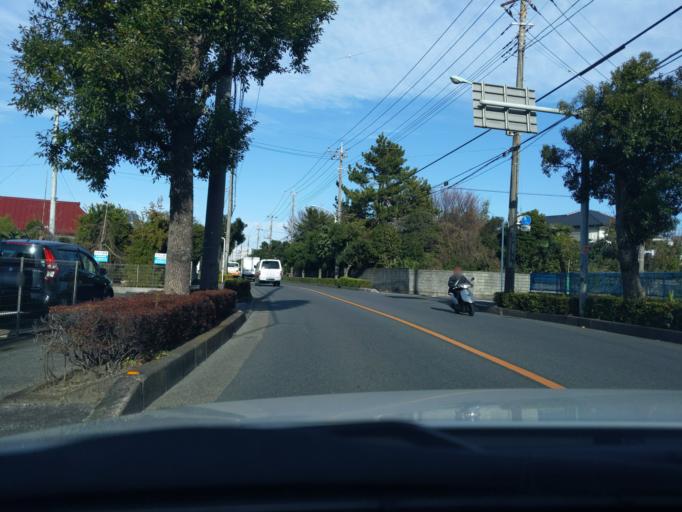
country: JP
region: Saitama
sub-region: Kawaguchi-shi
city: Hatogaya-honcho
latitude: 35.8157
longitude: 139.7539
